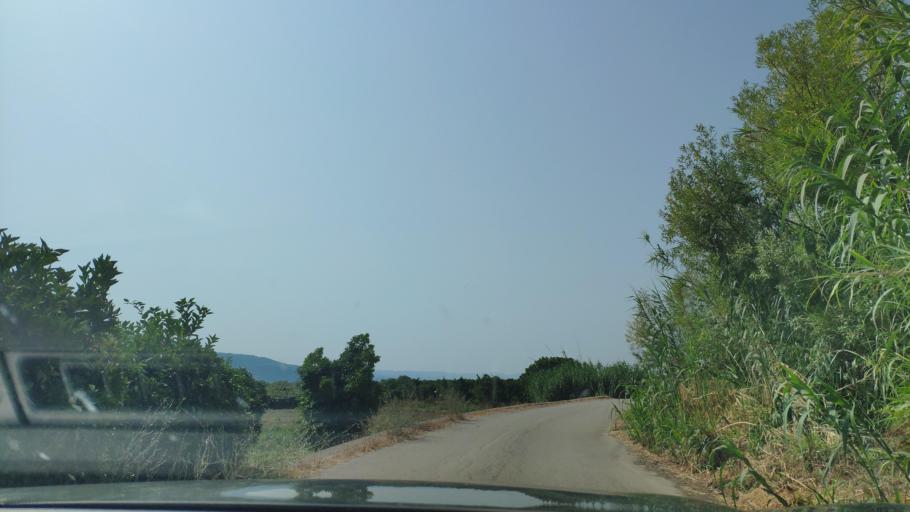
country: GR
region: Epirus
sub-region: Nomos Artas
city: Kompoti
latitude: 39.0687
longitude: 21.0788
